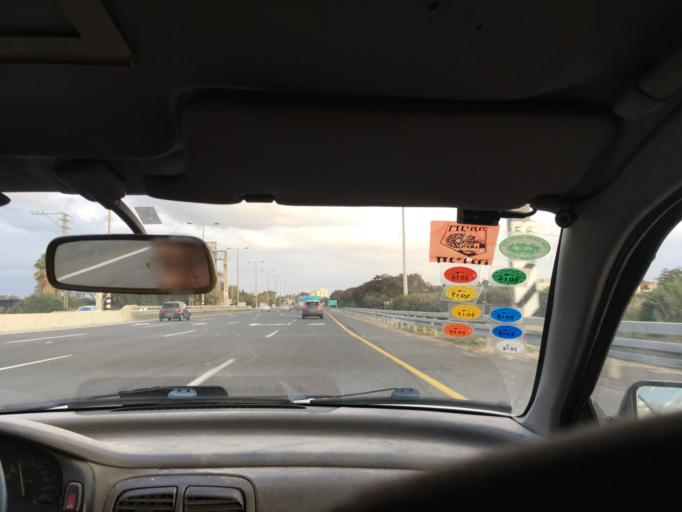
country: IL
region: Tel Aviv
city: Ramat HaSharon
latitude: 32.1381
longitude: 34.8220
